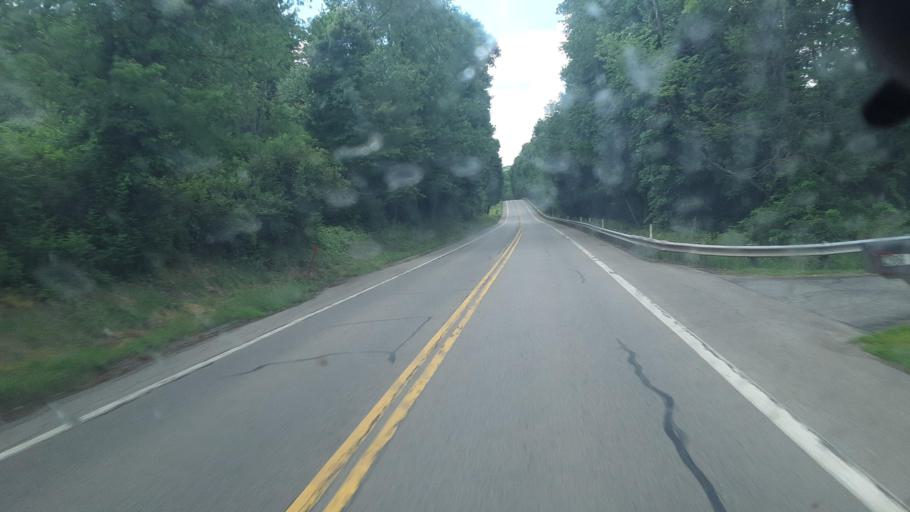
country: US
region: Pennsylvania
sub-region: Butler County
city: Slippery Rock
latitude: 41.0041
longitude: -80.1729
